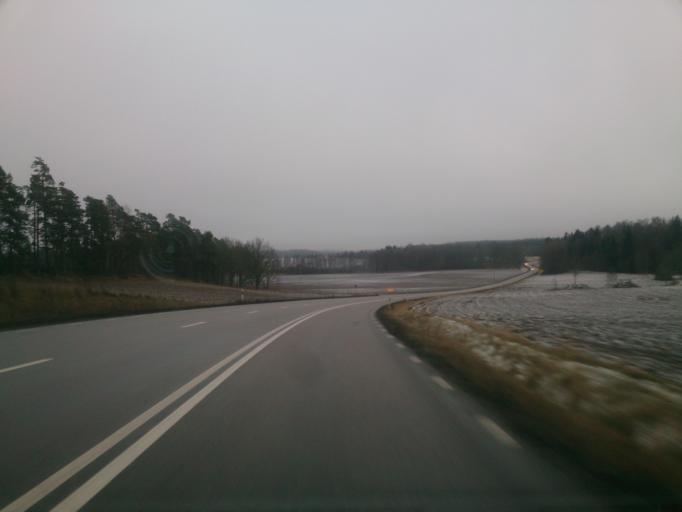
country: SE
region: OEstergoetland
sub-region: Atvidabergs Kommun
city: Atvidaberg
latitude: 58.2606
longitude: 15.9265
